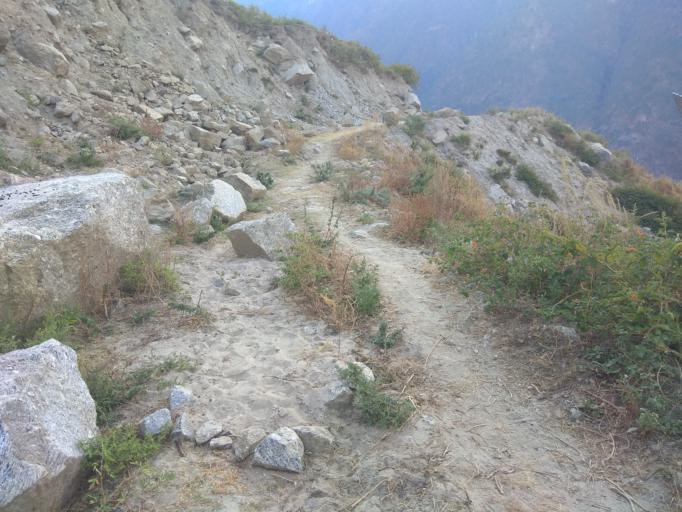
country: NP
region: Far Western
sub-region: Seti Zone
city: Achham
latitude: 29.2313
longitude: 81.6456
